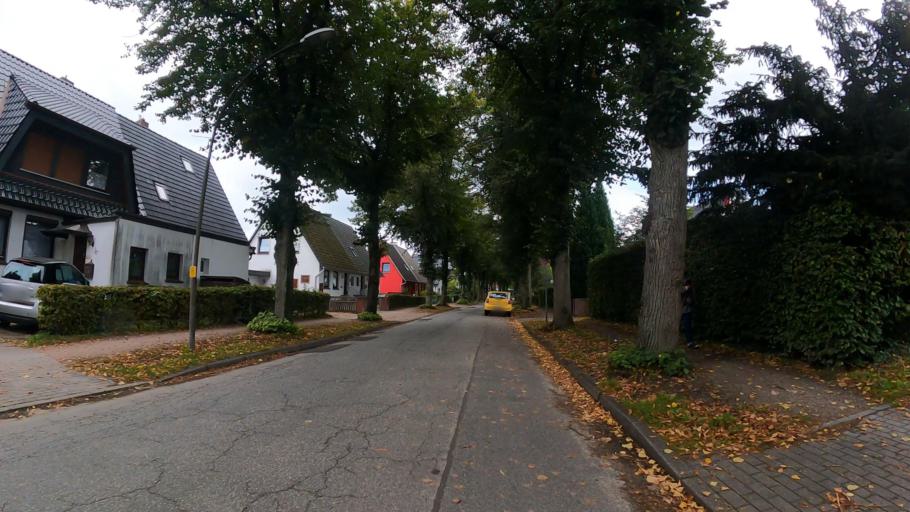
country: DE
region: Schleswig-Holstein
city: Tornesch
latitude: 53.6958
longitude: 9.7214
